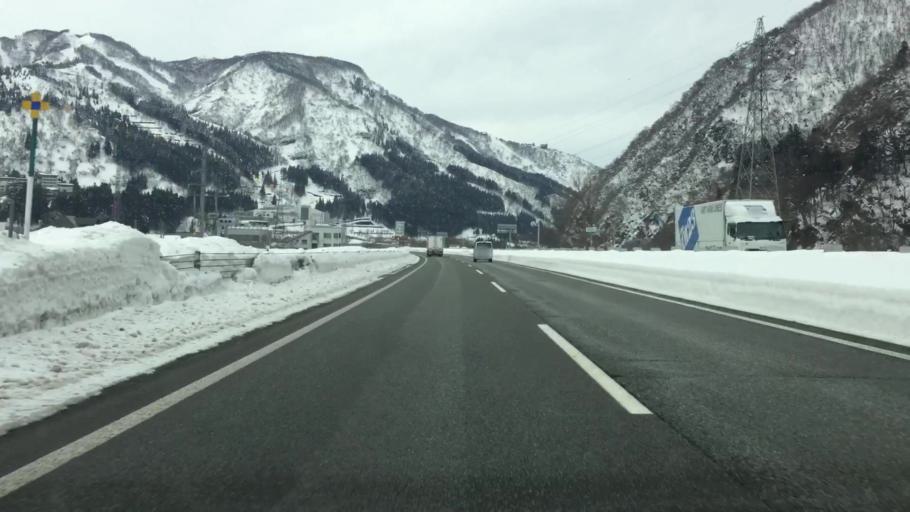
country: JP
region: Niigata
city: Shiozawa
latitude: 36.9423
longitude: 138.8121
